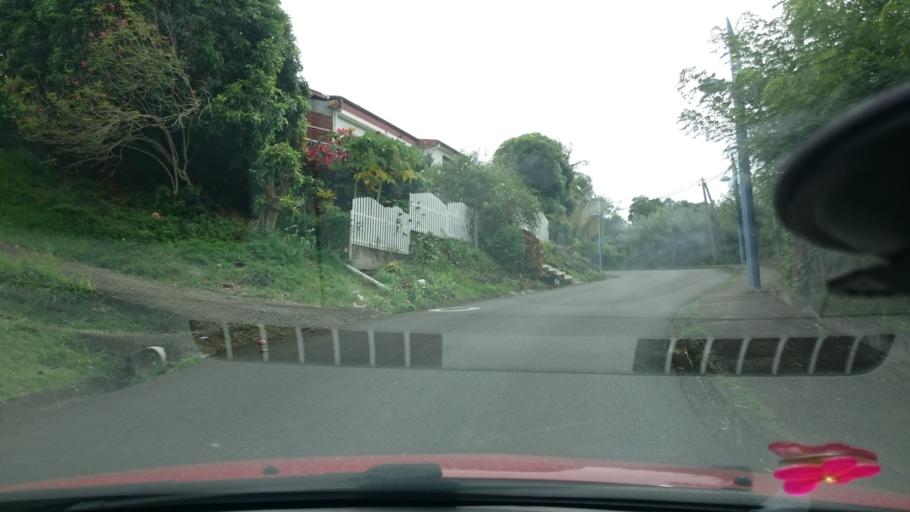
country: MQ
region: Martinique
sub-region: Martinique
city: Riviere-Pilote
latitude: 14.4859
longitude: -60.9091
